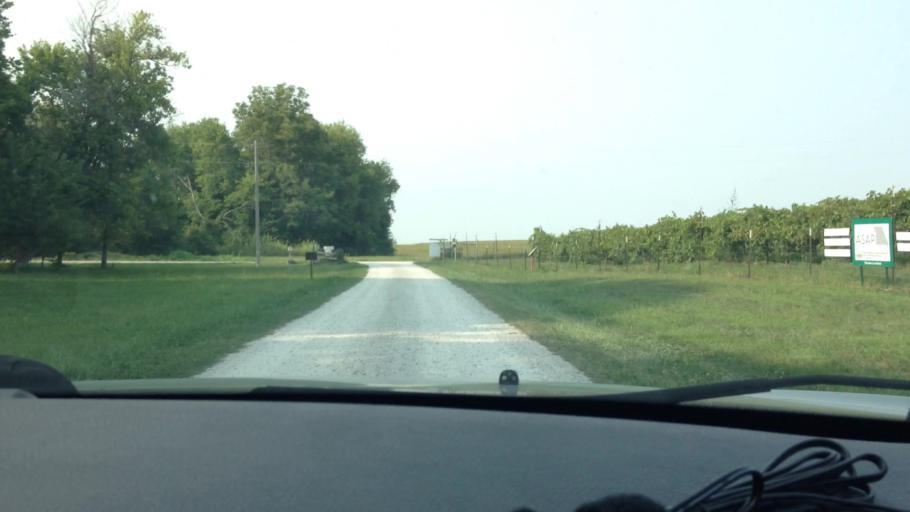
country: US
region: Missouri
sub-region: Platte County
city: Platte City
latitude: 39.4327
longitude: -94.7765
